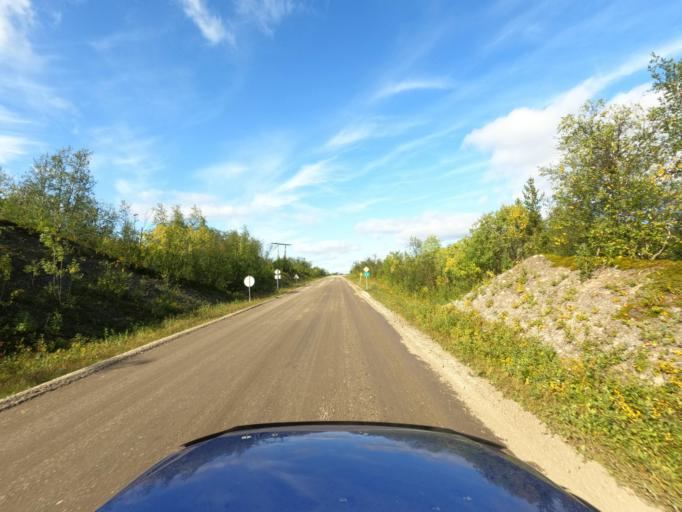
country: NO
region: Finnmark Fylke
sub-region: Porsanger
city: Lakselv
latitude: 69.8781
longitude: 25.0261
